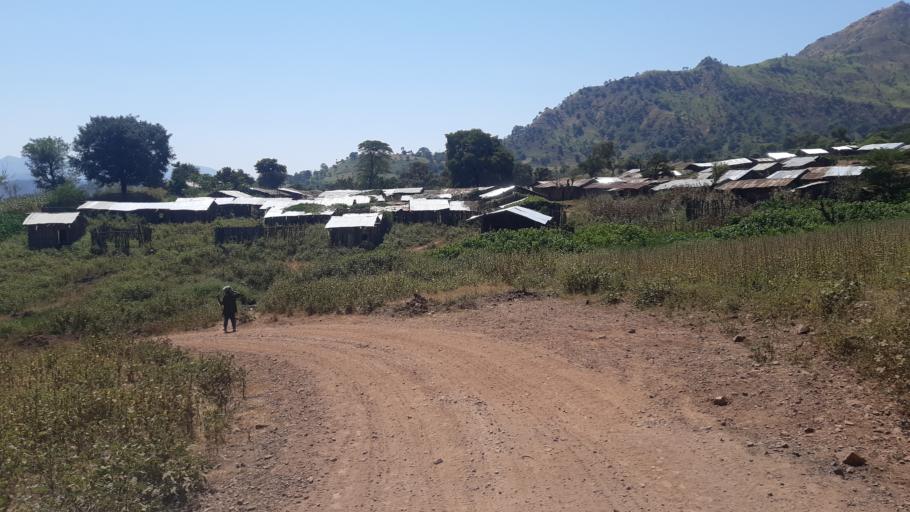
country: ET
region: Amhara
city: Dabat
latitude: 13.2470
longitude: 37.5260
